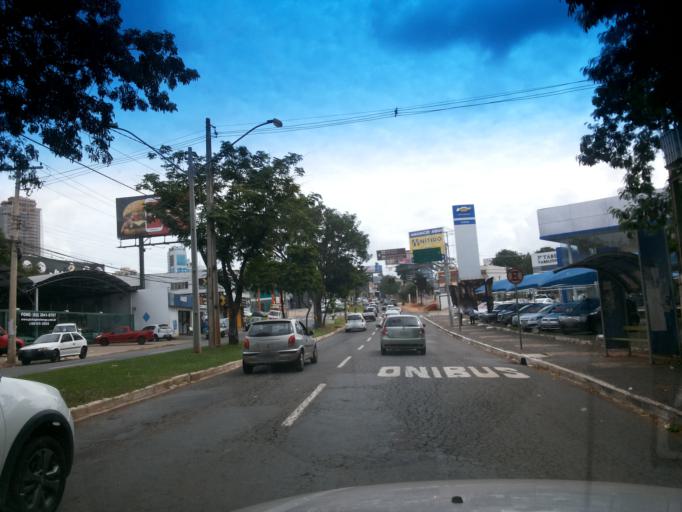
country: BR
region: Goias
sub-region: Goiania
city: Goiania
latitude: -16.6995
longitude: -49.2477
